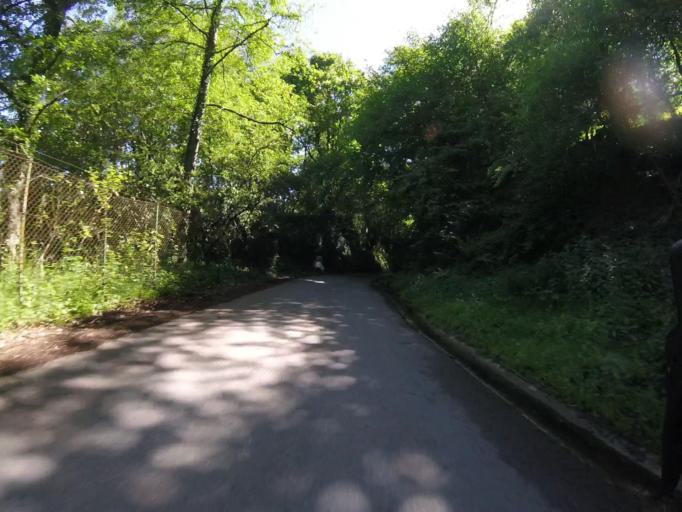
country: ES
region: Navarre
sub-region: Provincia de Navarra
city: Bera
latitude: 43.2742
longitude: -1.7089
